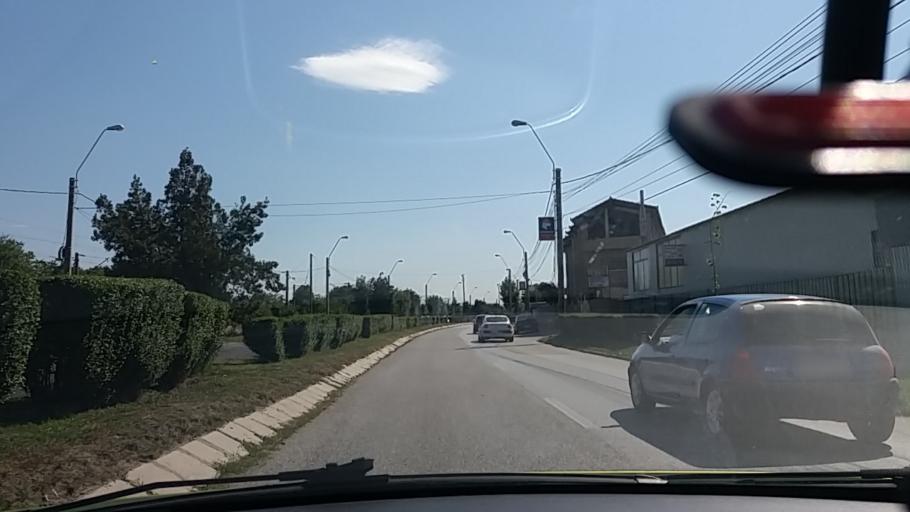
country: RO
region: Hunedoara
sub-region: Municipiul Deva
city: Deva
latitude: 45.8918
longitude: 22.9046
